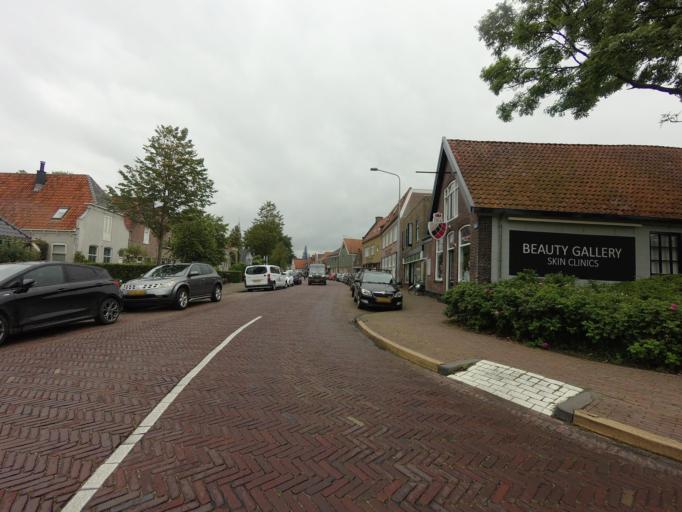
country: NL
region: North Holland
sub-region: Gemeente Schagen
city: Schagen
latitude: 52.7851
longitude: 4.7930
